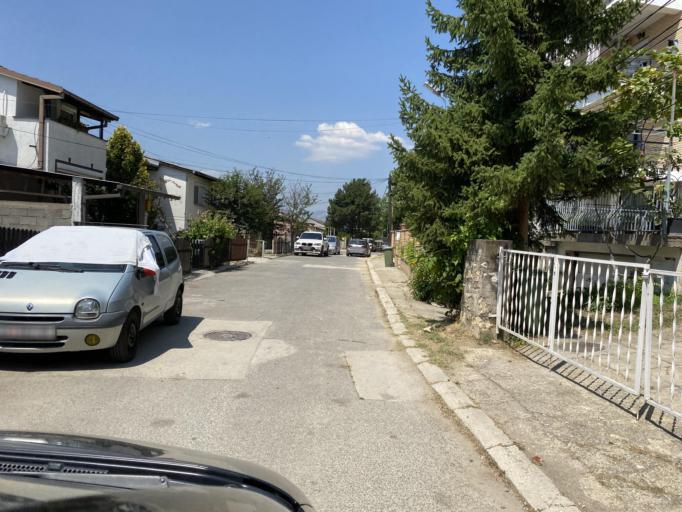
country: MK
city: Radishani
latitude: 42.0588
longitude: 21.4469
